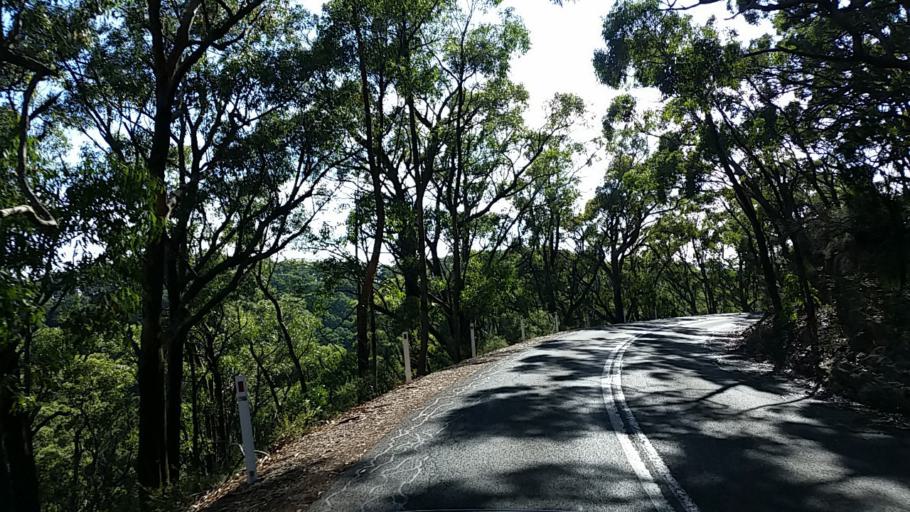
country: AU
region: South Australia
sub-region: Adelaide Hills
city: Crafers
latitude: -34.9665
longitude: 138.7107
